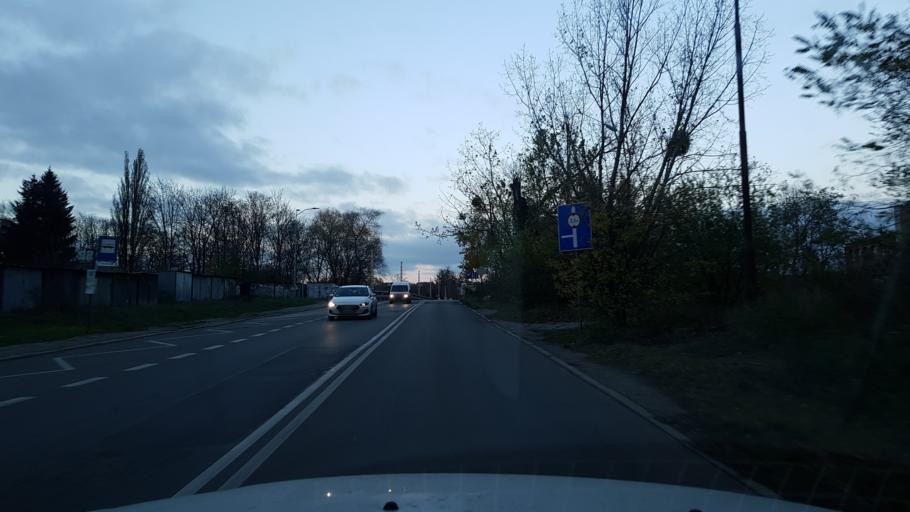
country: PL
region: West Pomeranian Voivodeship
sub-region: Szczecin
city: Szczecin
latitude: 53.4489
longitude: 14.5776
